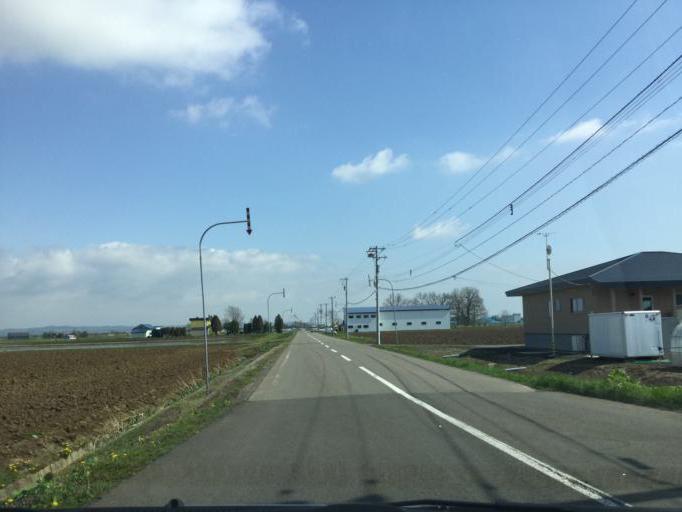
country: JP
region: Hokkaido
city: Iwamizawa
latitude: 43.1629
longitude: 141.6791
